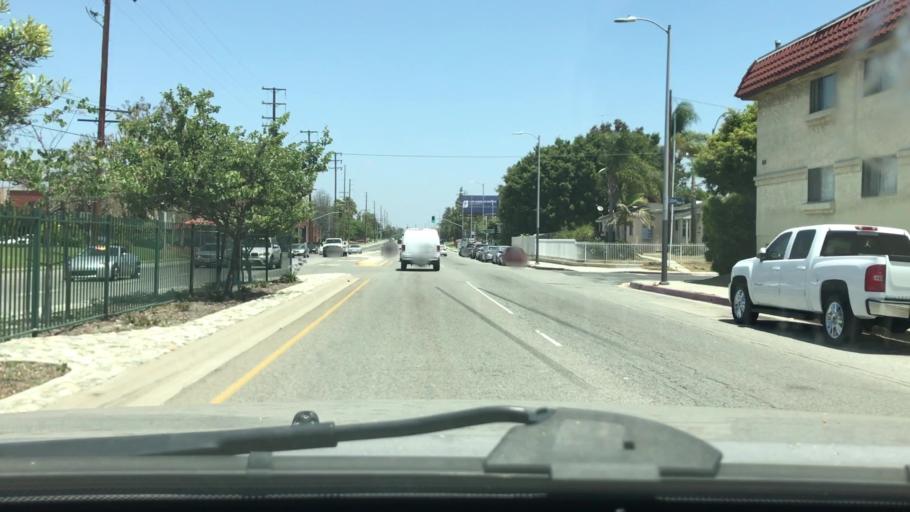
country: US
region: California
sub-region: Los Angeles County
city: West Carson
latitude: 33.8453
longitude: -118.3092
